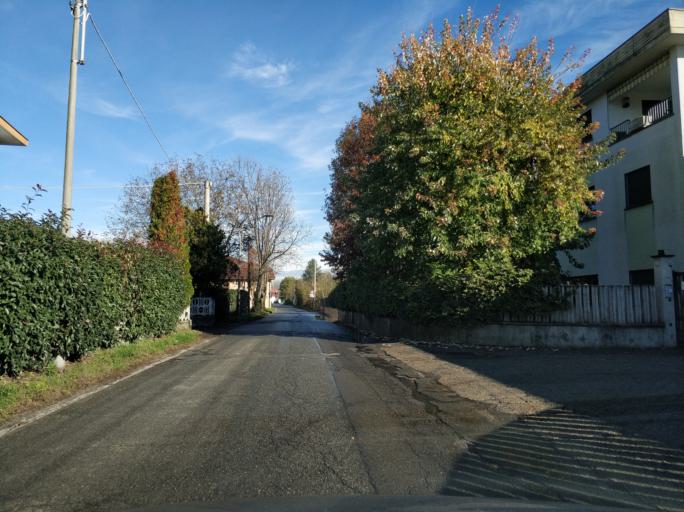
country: IT
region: Piedmont
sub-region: Provincia di Torino
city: Cirie
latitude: 45.2286
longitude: 7.5876
